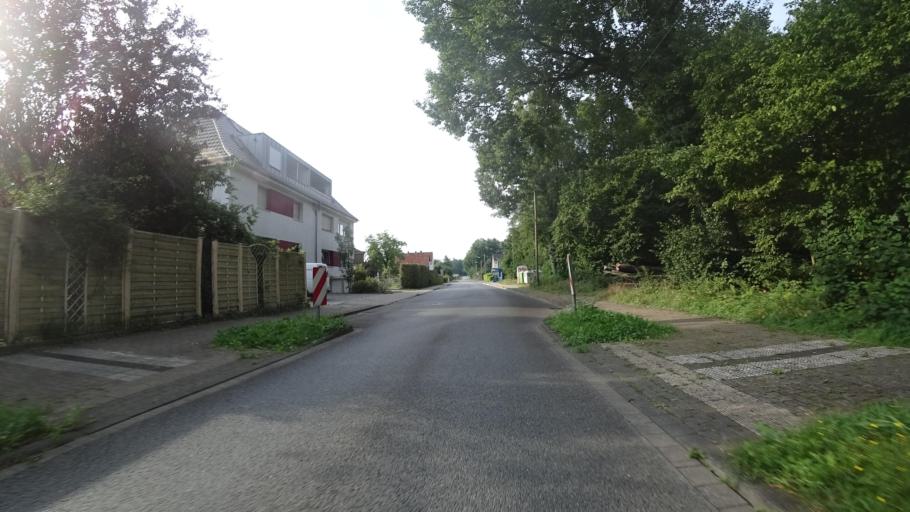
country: DE
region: North Rhine-Westphalia
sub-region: Regierungsbezirk Detmold
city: Steinhagen
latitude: 51.9633
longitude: 8.4682
